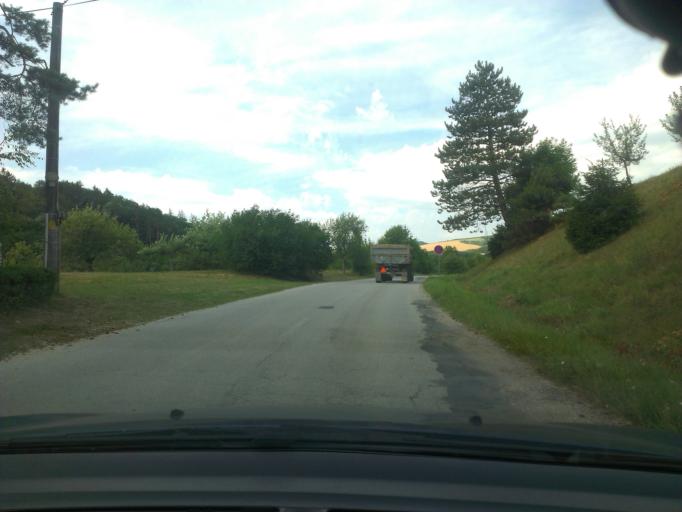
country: SK
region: Trenciansky
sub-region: Okres Myjava
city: Myjava
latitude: 48.7768
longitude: 17.5784
